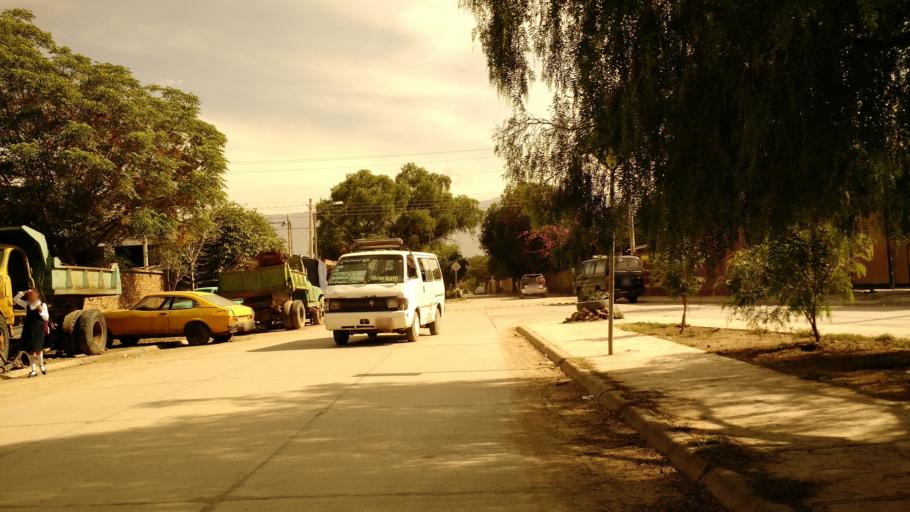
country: BO
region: Cochabamba
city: Cochabamba
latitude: -17.4362
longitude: -66.1600
